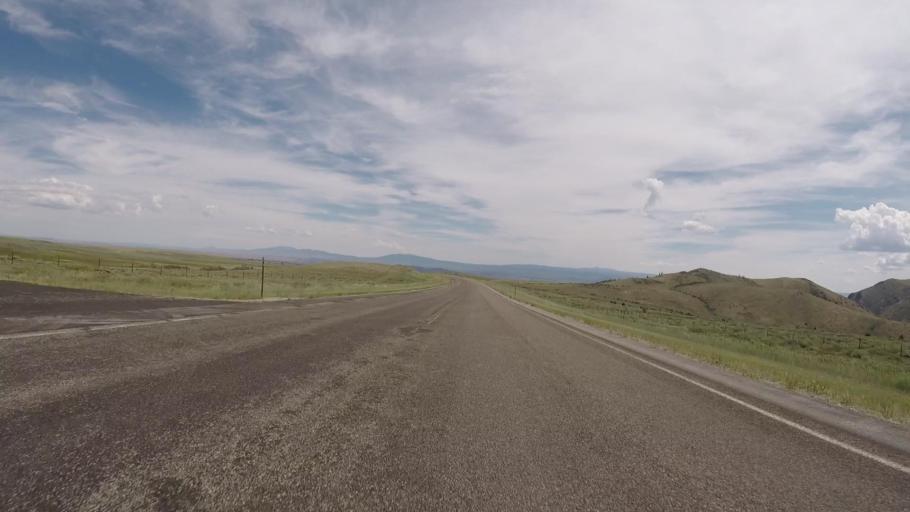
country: US
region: Wyoming
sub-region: Carbon County
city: Saratoga
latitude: 41.1867
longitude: -106.8578
